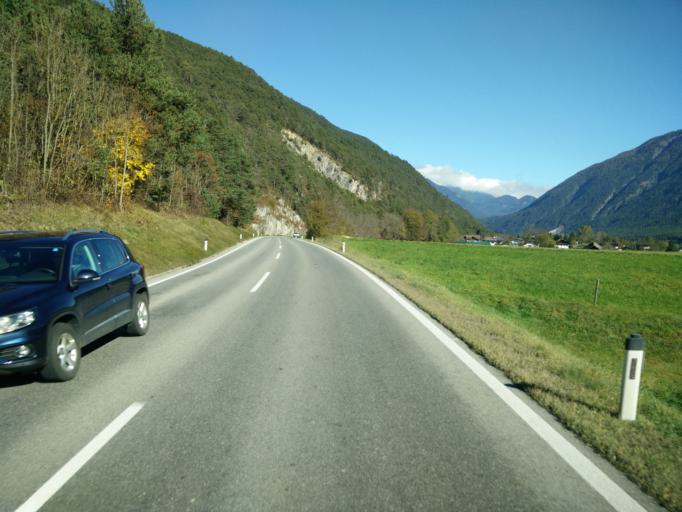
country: AT
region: Tyrol
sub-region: Politischer Bezirk Imst
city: Tarrenz
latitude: 47.2746
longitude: 10.7859
